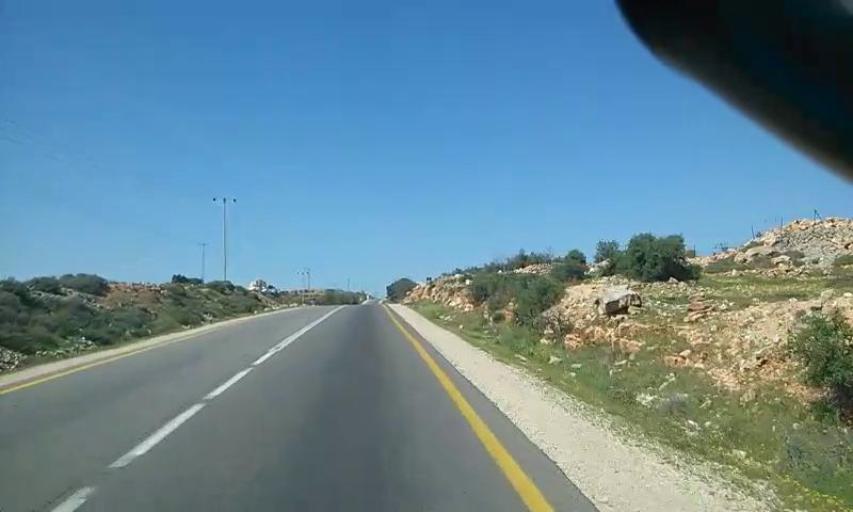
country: PS
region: West Bank
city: Jurat ash Sham`ah
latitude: 31.6483
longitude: 35.1699
